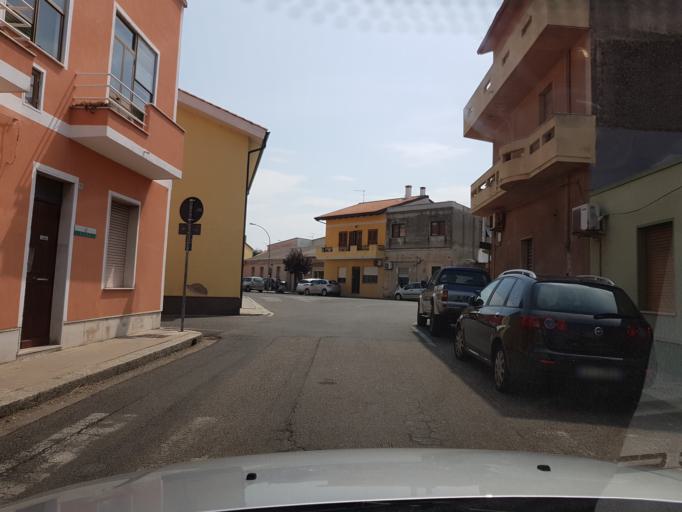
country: IT
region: Sardinia
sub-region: Provincia di Oristano
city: Oristano
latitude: 39.9066
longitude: 8.5971
